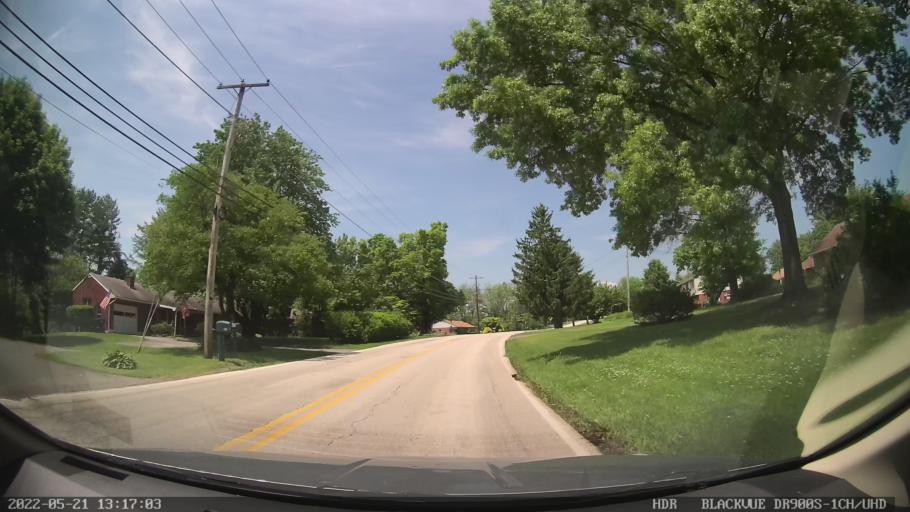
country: US
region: Pennsylvania
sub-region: Montgomery County
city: Gilbertsville
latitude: 40.3553
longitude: -75.5899
